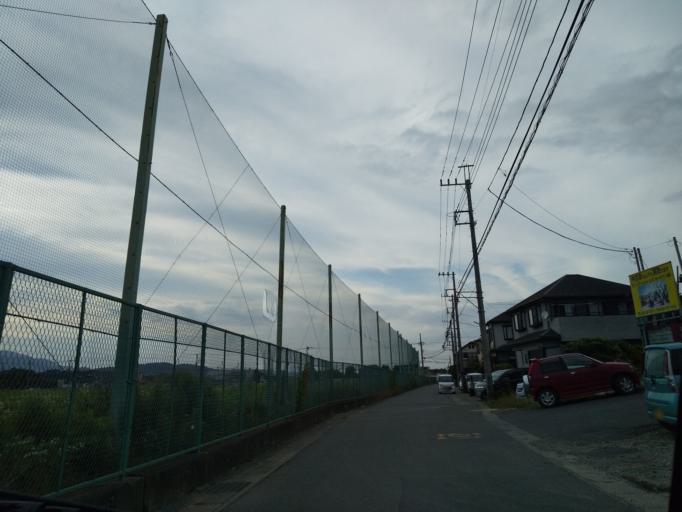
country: JP
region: Kanagawa
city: Zama
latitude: 35.4756
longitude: 139.3597
